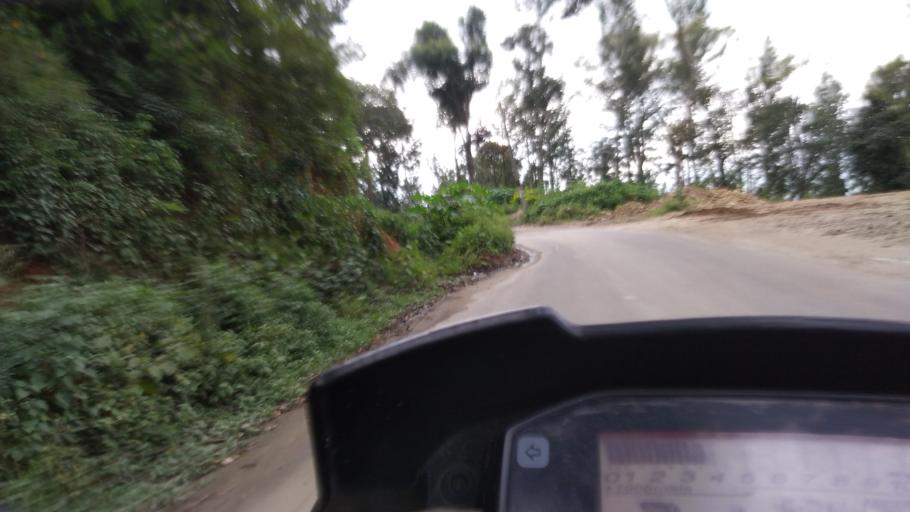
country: IN
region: Tamil Nadu
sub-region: Theni
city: Bodinayakkanur
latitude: 10.0077
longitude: 77.2325
